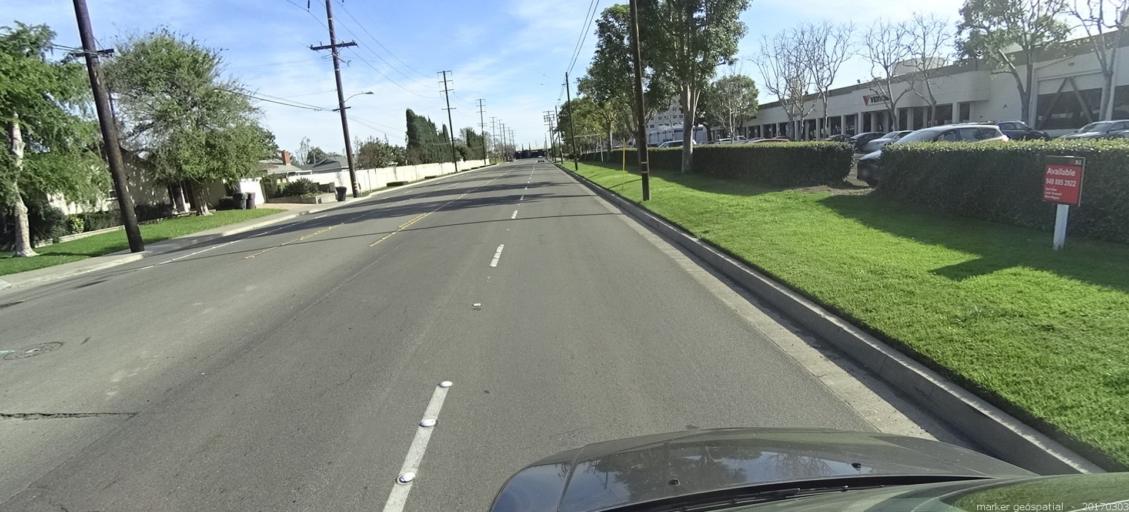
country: US
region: California
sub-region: Orange County
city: Anaheim
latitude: 33.8219
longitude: -117.8974
